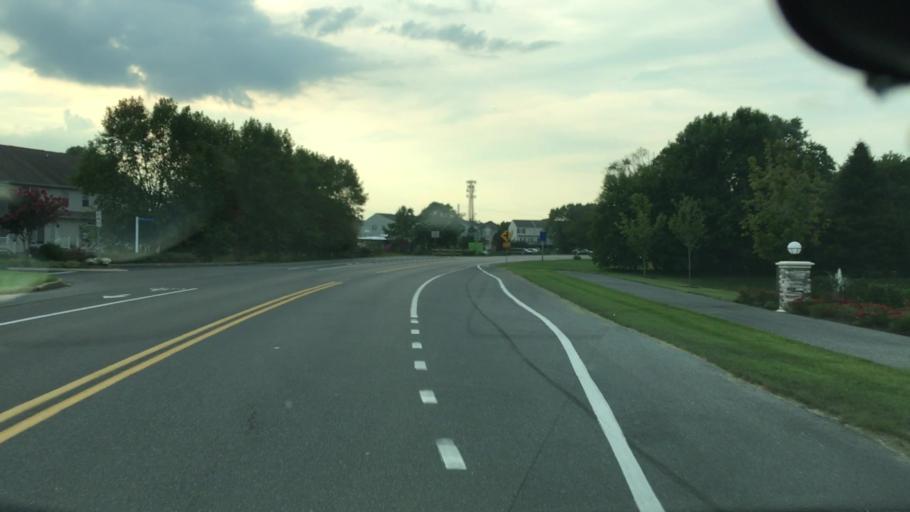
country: US
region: Delaware
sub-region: Sussex County
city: Ocean View
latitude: 38.5263
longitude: -75.0806
